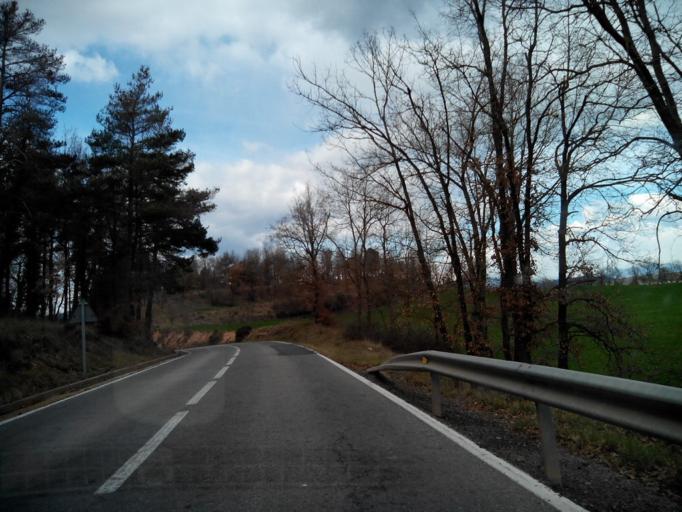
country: ES
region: Catalonia
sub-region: Provincia de Barcelona
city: Olost
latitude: 41.9685
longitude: 2.1409
